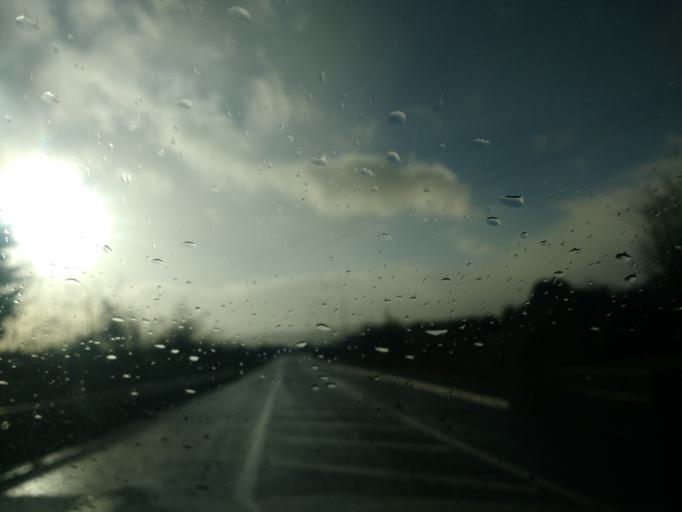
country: IE
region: Ulster
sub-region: County Donegal
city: Letterkenny
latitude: 54.9621
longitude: -7.6912
